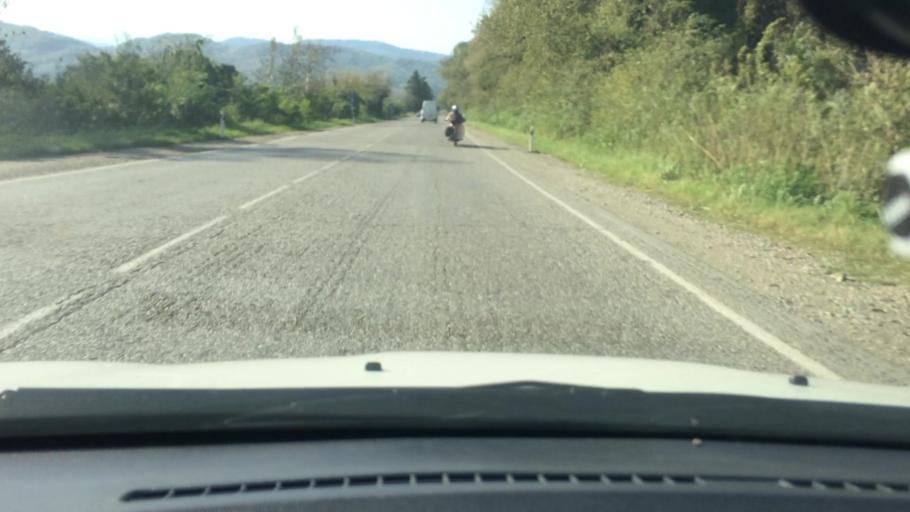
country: GE
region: Imereti
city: Samtredia
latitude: 42.1259
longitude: 42.3349
